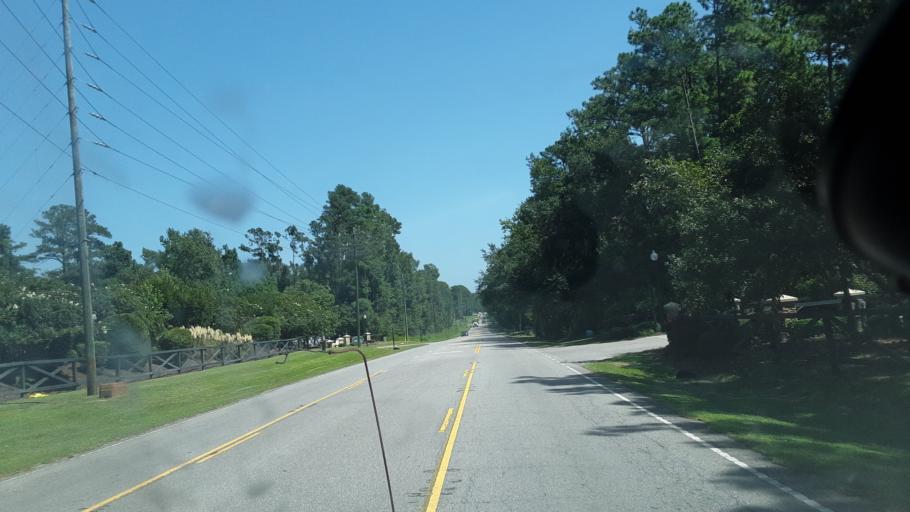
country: US
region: South Carolina
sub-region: Horry County
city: Forestbrook
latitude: 33.8311
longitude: -78.8895
